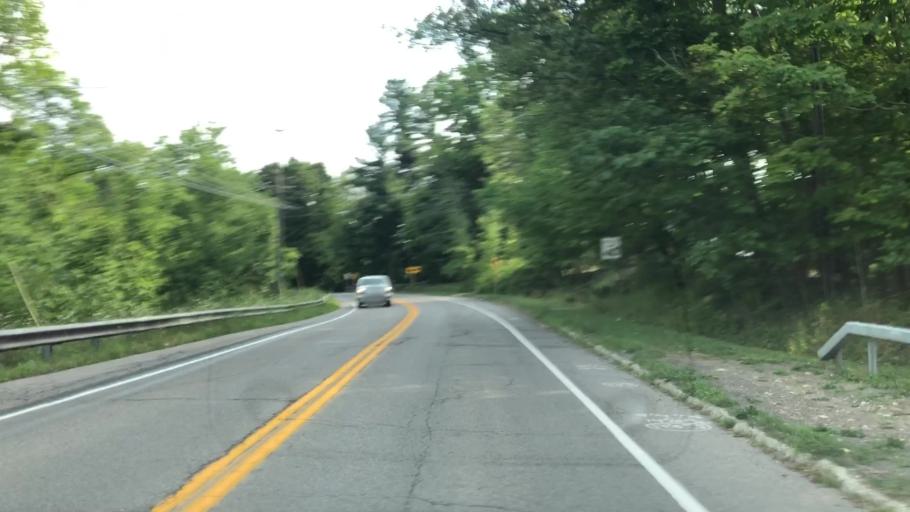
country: US
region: New York
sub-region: Erie County
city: Elma Center
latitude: 42.8480
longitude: -78.6412
